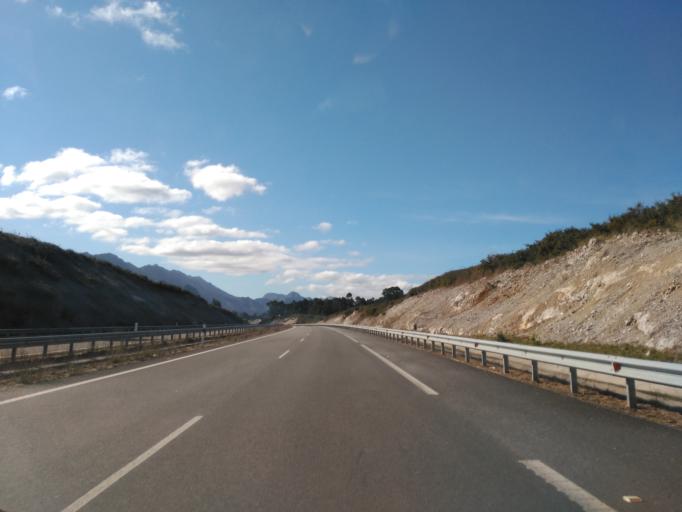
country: ES
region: Asturias
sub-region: Province of Asturias
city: Llanes
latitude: 43.4029
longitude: -4.6864
